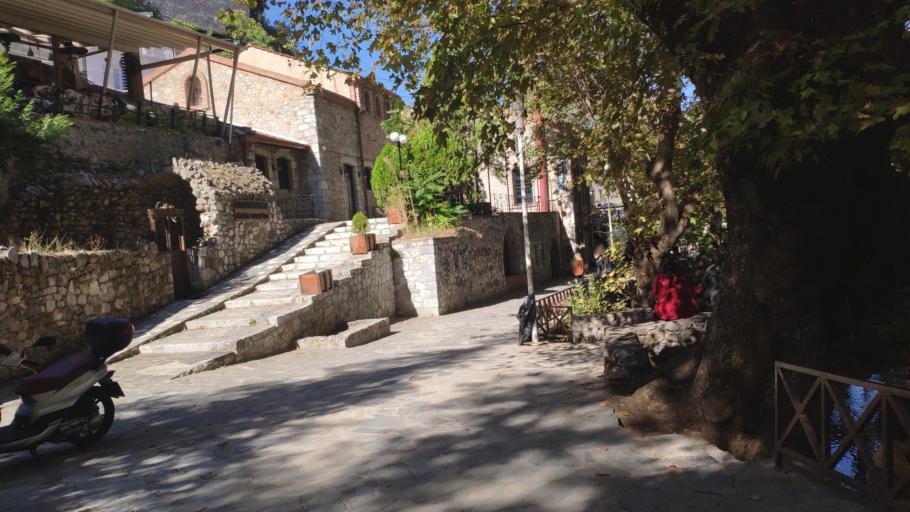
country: GR
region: Central Greece
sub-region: Nomos Voiotias
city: Livadeia
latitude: 38.4323
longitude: 22.8749
